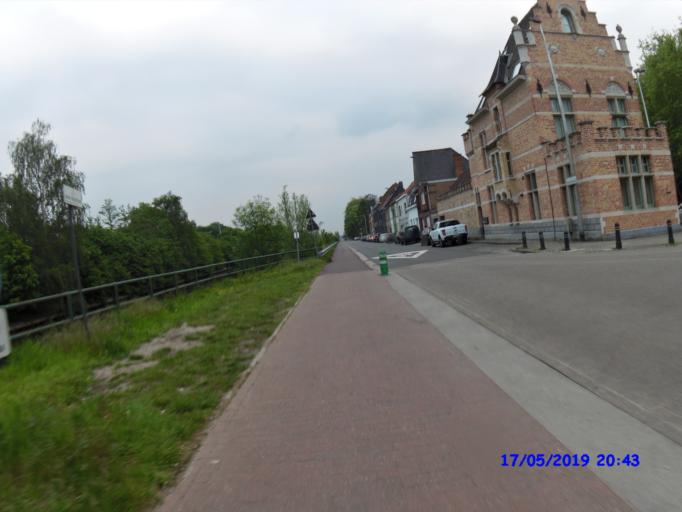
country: BE
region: Flanders
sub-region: Provincie Oost-Vlaanderen
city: Evergem
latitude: 51.0776
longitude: 3.6777
